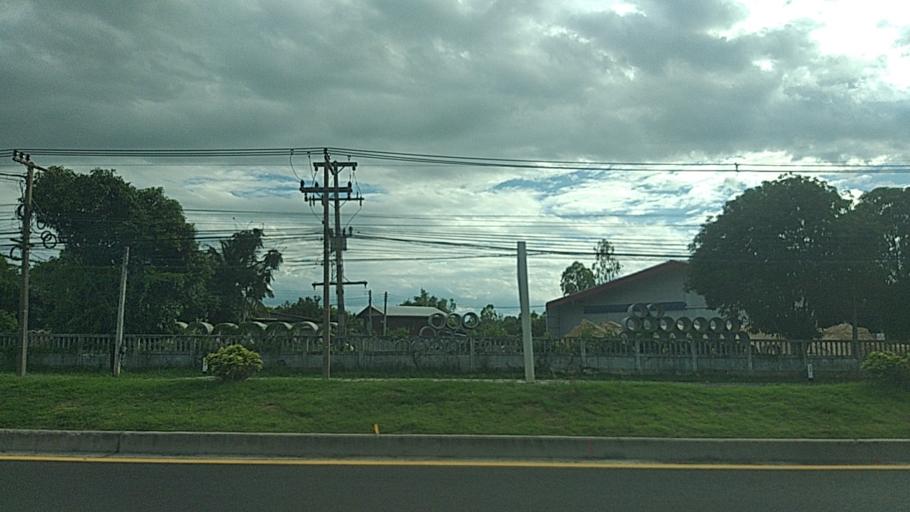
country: TH
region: Surin
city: Prasat
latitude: 14.6199
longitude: 103.4135
